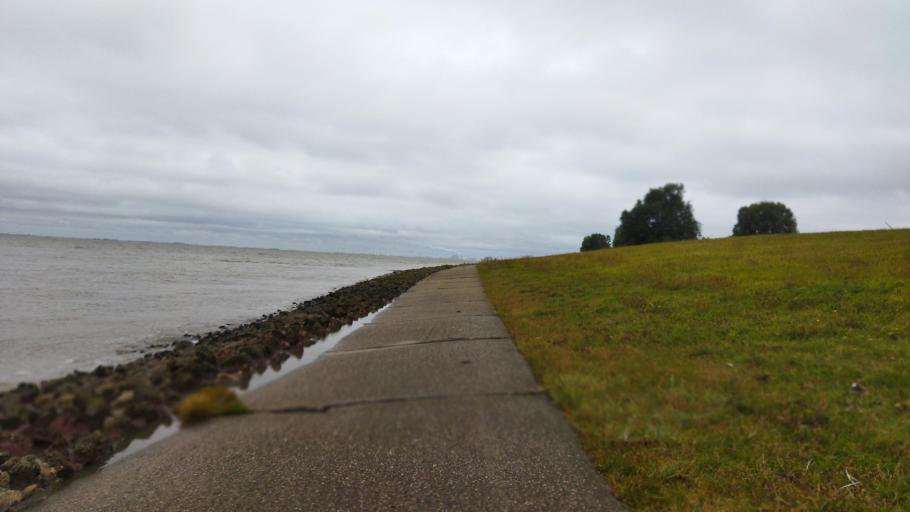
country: NL
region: Groningen
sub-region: Gemeente Delfzijl
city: Delfzijl
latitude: 53.3400
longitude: 7.0184
